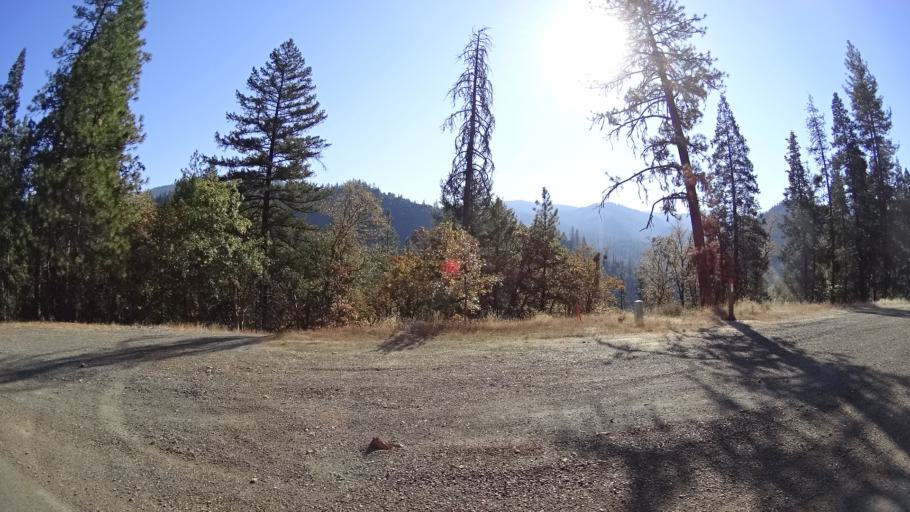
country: US
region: California
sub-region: Siskiyou County
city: Happy Camp
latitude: 41.7310
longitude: -123.0108
